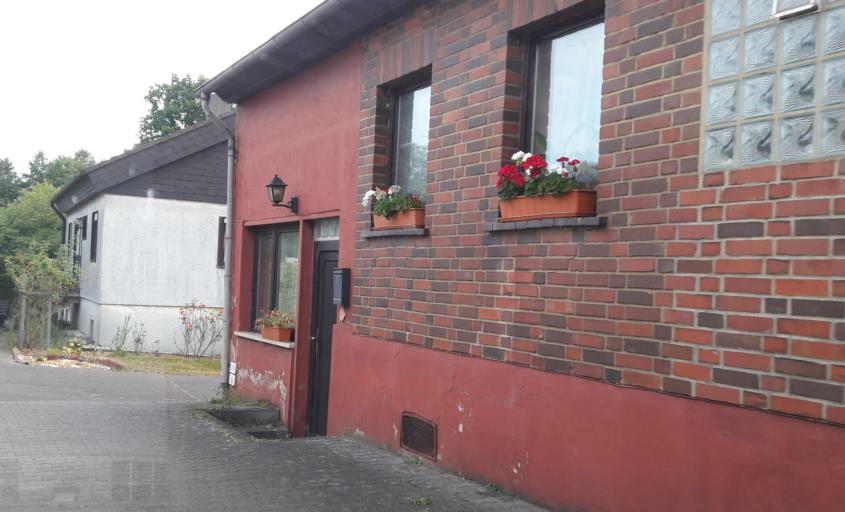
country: DE
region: Rheinland-Pfalz
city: Dienstweiler
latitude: 49.6089
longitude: 7.1755
